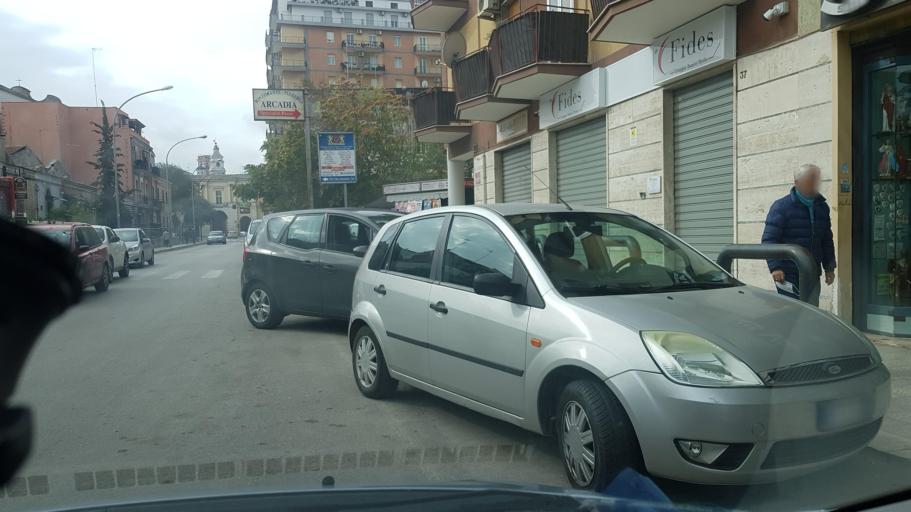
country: IT
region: Apulia
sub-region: Provincia di Foggia
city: Foggia
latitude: 41.4668
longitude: 15.5463
